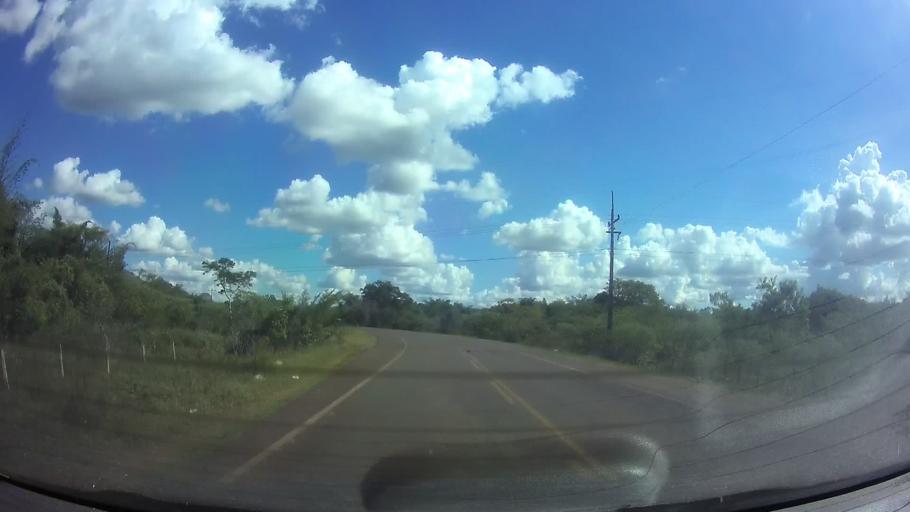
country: PY
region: Paraguari
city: Sapucai
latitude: -25.6835
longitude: -56.8635
